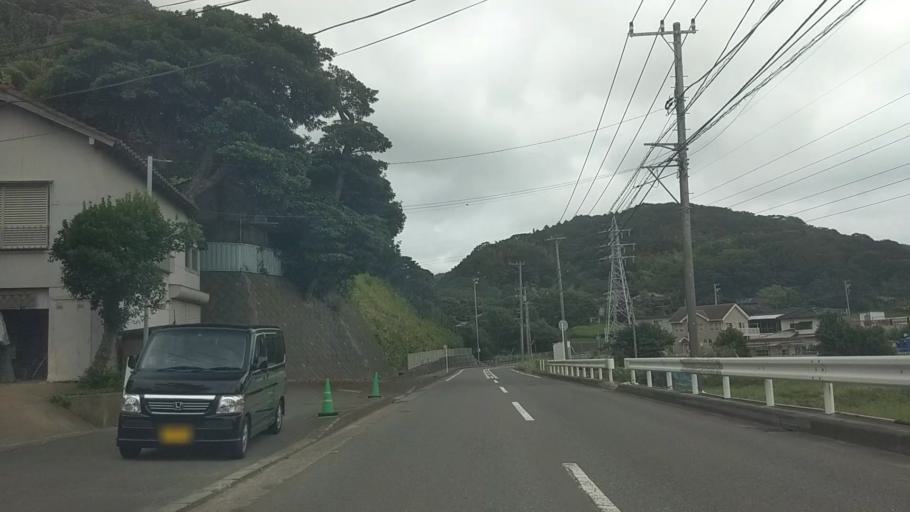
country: JP
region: Kanagawa
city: Yokosuka
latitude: 35.2339
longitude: 139.6342
